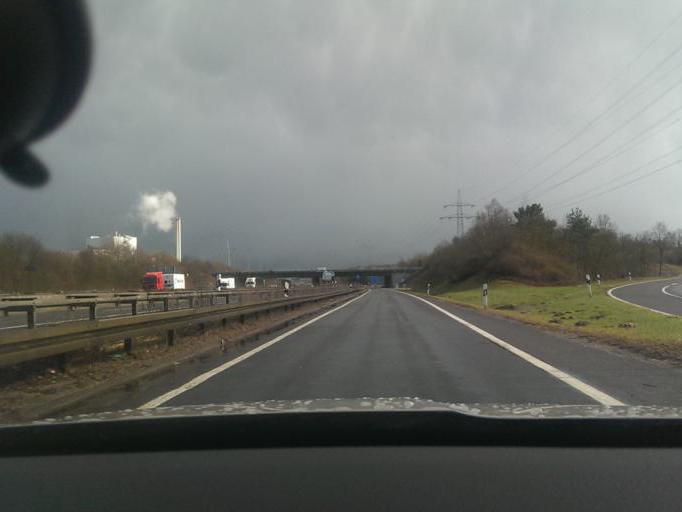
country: DE
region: Lower Saxony
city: Isernhagen Farster Bauerschaft
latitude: 52.4141
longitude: 9.8444
